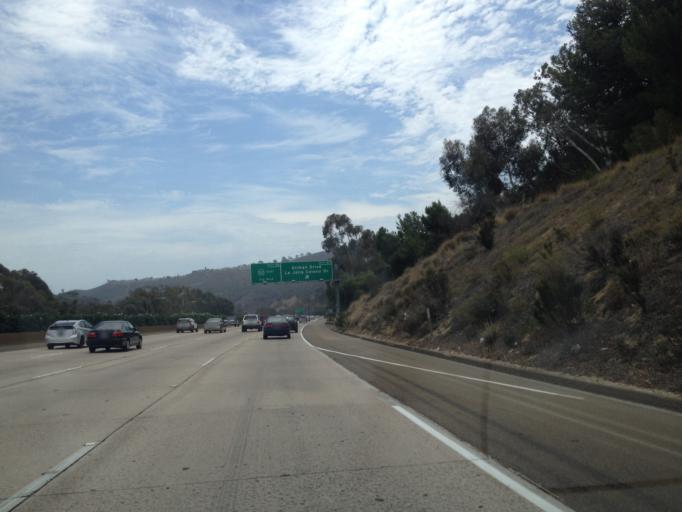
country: US
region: California
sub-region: San Diego County
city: La Jolla
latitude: 32.8552
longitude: -117.2315
